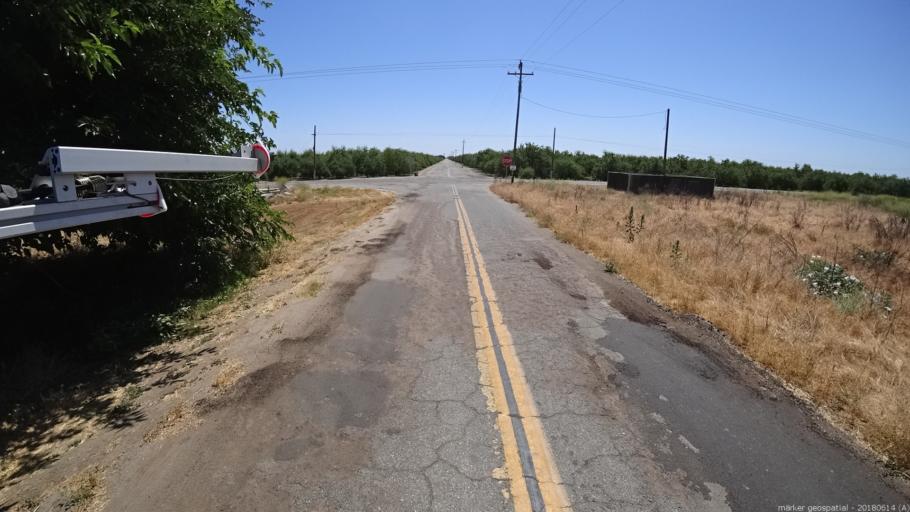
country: US
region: California
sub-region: Madera County
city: Fairmead
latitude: 36.9892
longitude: -120.2028
